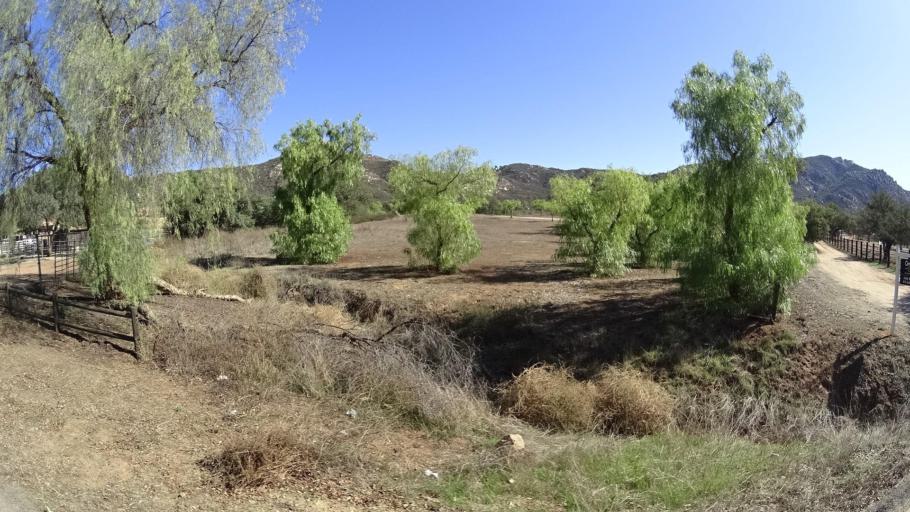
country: US
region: California
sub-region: San Diego County
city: Jamul
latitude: 32.7262
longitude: -116.8157
